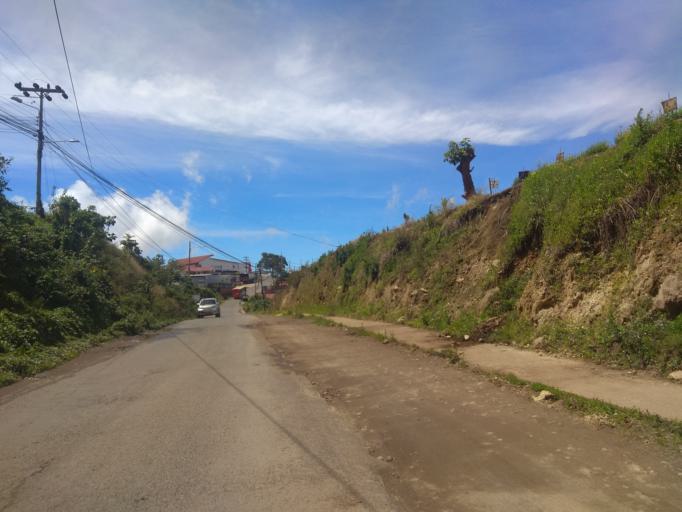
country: CR
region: Cartago
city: Cot
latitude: 9.9144
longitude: -83.8898
